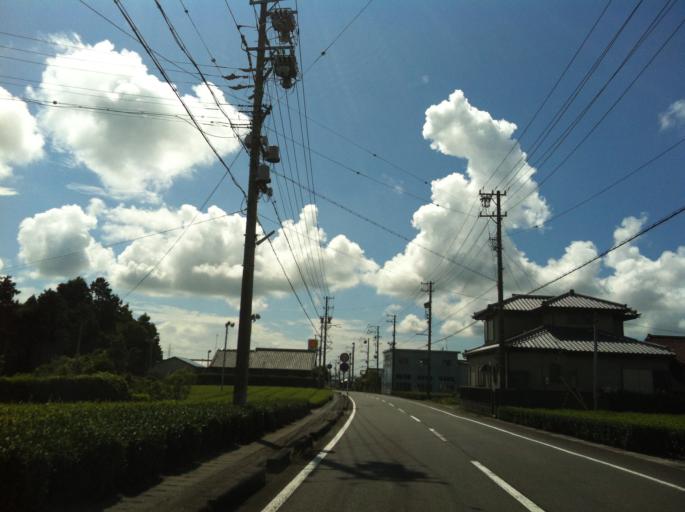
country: JP
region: Shizuoka
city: Kanaya
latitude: 34.7981
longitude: 138.1367
